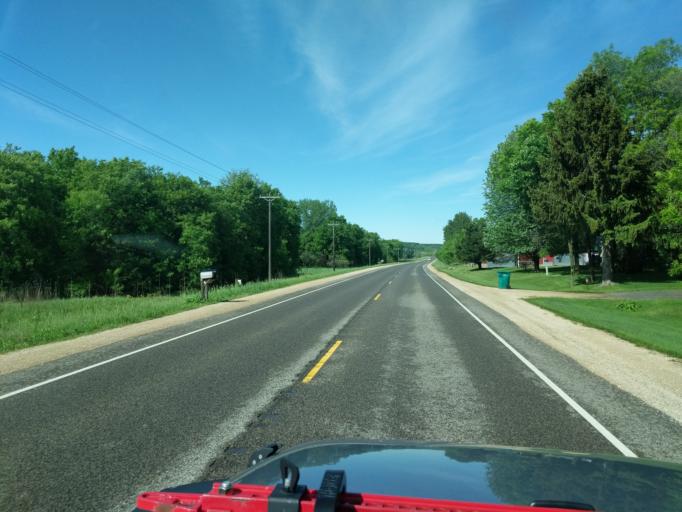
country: US
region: Wisconsin
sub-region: Pierce County
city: River Falls
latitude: 44.8556
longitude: -92.5381
